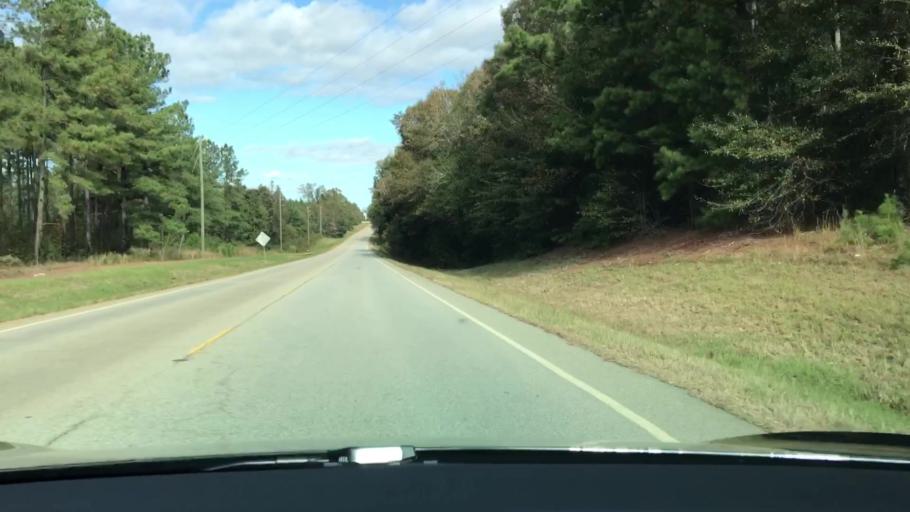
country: US
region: Georgia
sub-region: Jefferson County
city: Louisville
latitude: 33.0912
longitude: -82.4164
